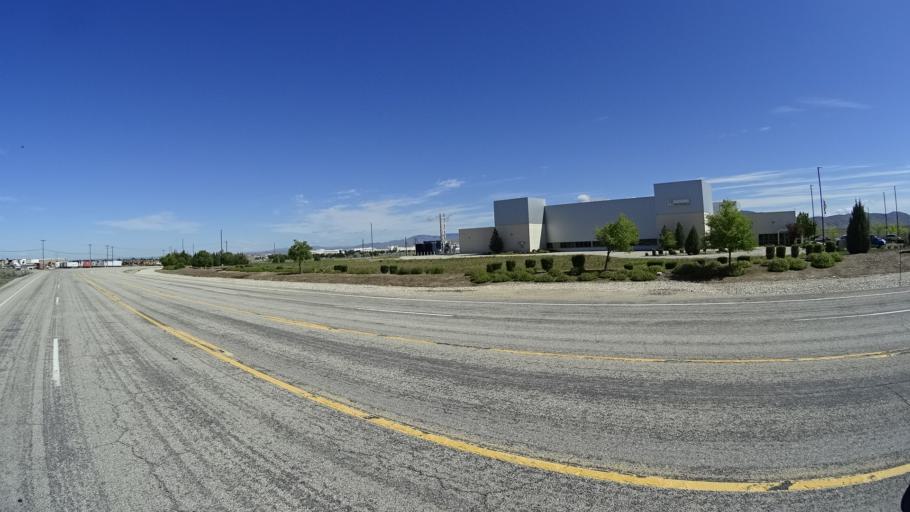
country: US
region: Idaho
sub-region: Ada County
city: Boise
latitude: 43.5110
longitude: -116.1411
